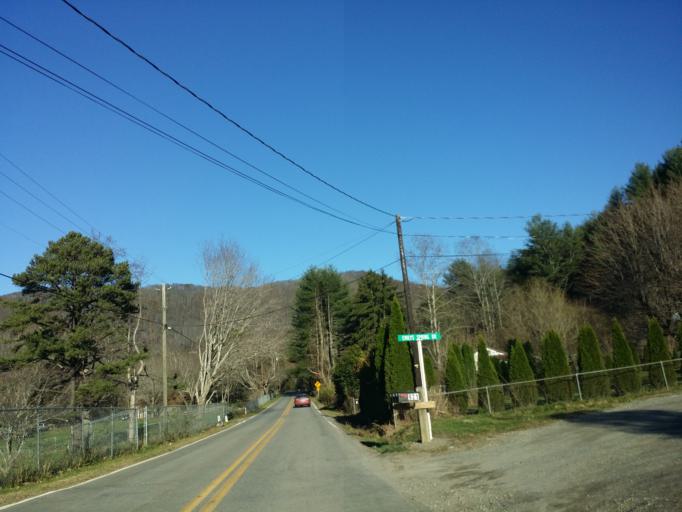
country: US
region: North Carolina
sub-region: Buncombe County
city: Swannanoa
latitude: 35.6318
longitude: -82.4249
